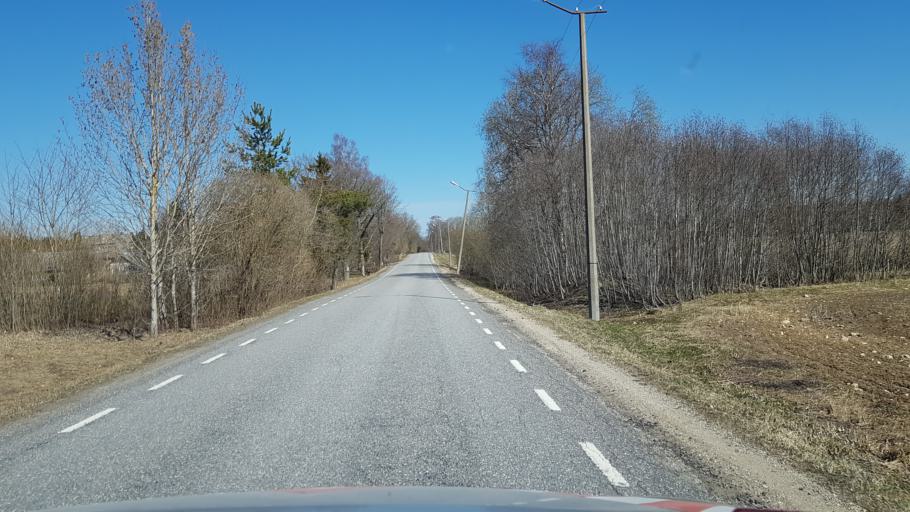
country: EE
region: Laeaene-Virumaa
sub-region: Tamsalu vald
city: Tamsalu
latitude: 59.0857
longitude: 26.1633
